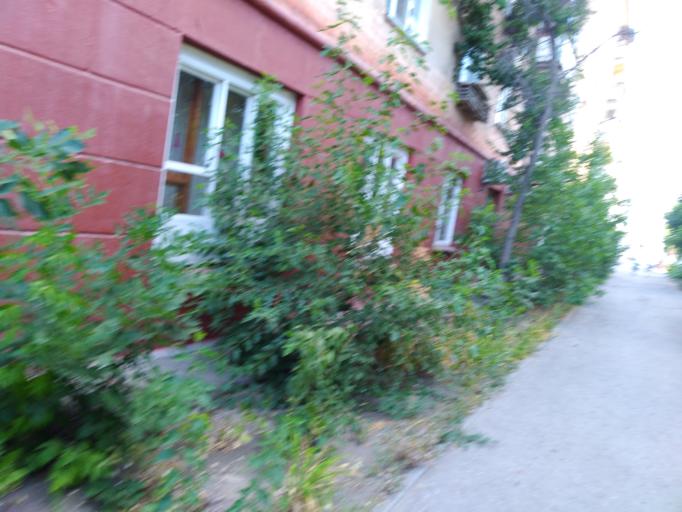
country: RU
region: Volgograd
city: Volgograd
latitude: 48.7138
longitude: 44.5324
